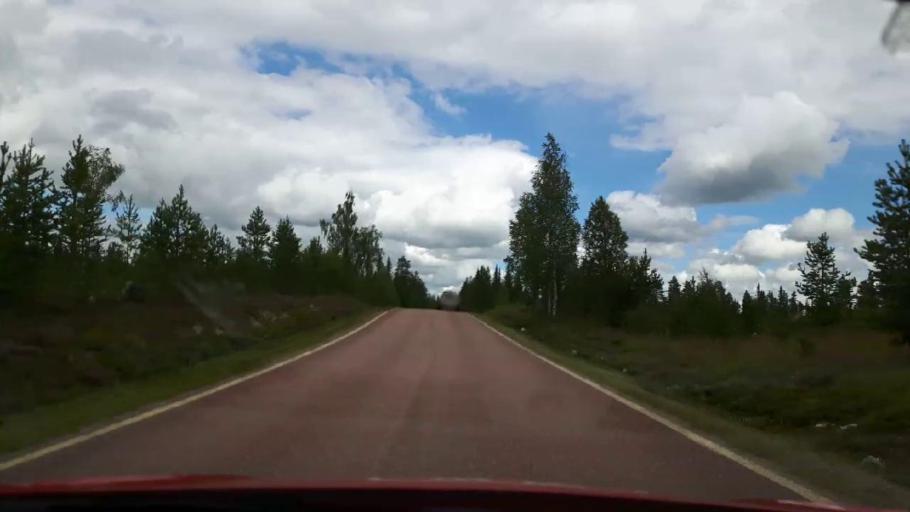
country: NO
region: Hedmark
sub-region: Trysil
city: Innbygda
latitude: 61.8777
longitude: 12.9680
